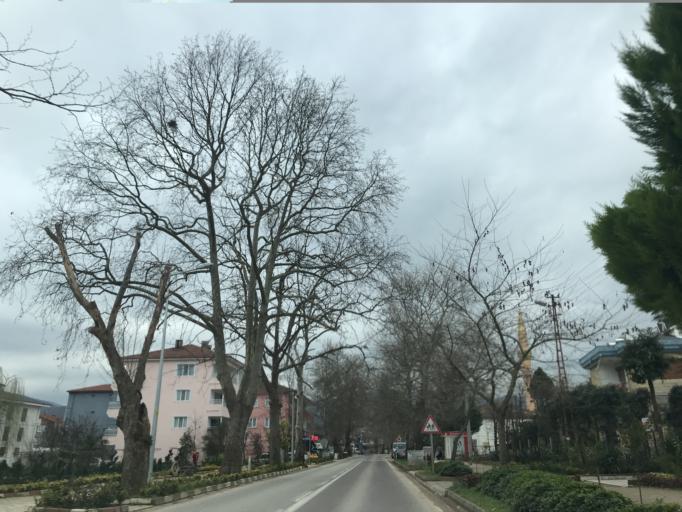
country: TR
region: Yalova
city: Kadikoy
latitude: 40.6206
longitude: 29.2189
